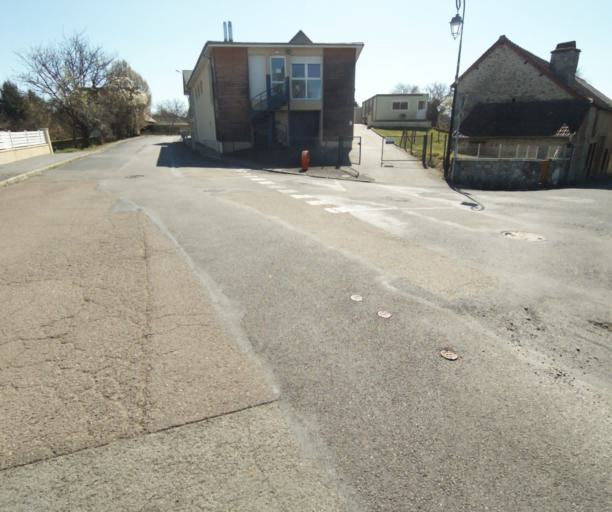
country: FR
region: Limousin
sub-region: Departement de la Correze
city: Saint-Mexant
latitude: 45.2862
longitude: 1.6582
